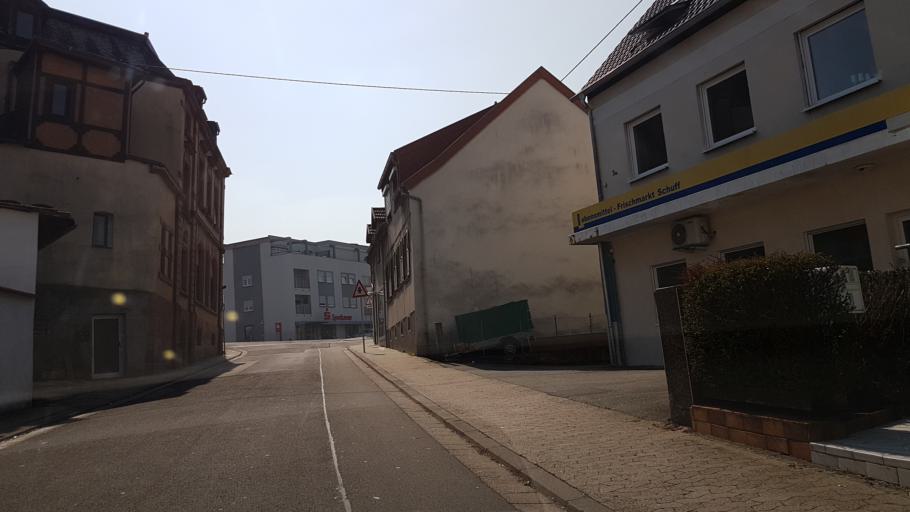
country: DE
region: Saarland
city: Quierschied
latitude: 49.3108
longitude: 7.0601
